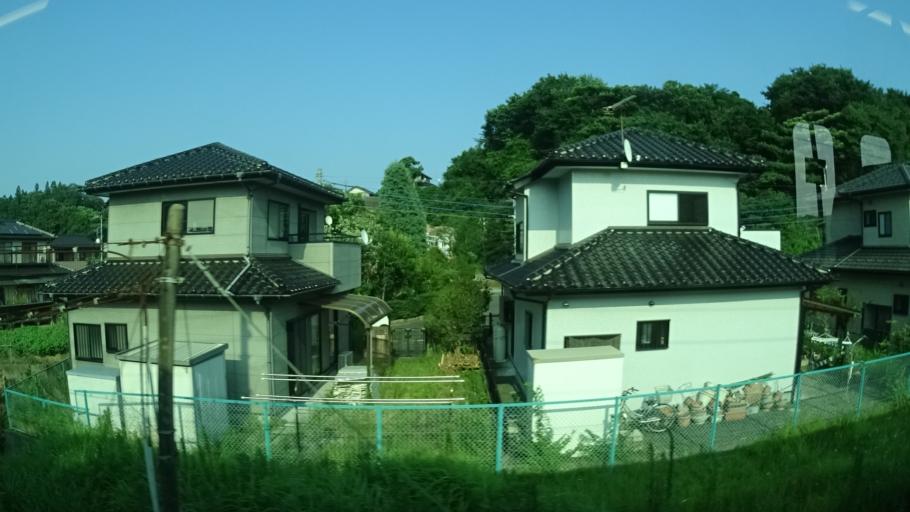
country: JP
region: Ibaraki
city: Kitaibaraki
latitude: 36.8541
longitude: 140.7792
